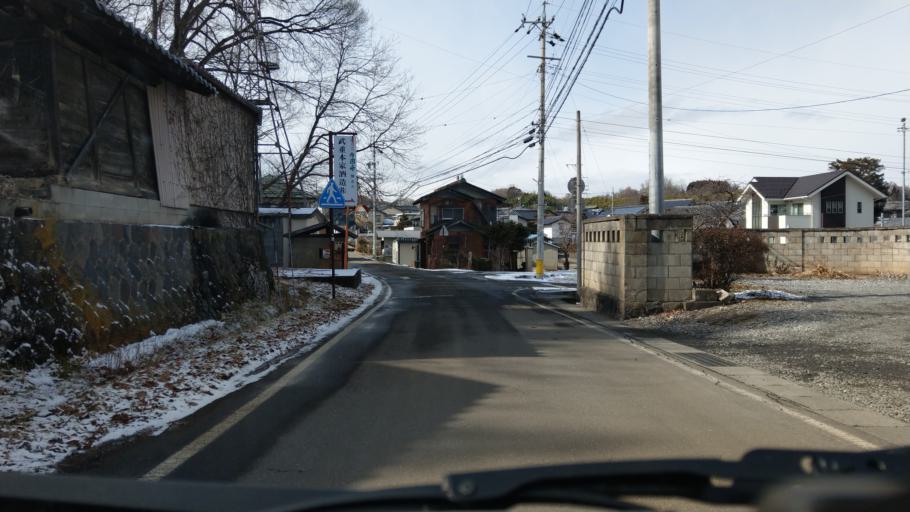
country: JP
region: Nagano
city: Kamimaruko
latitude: 36.2717
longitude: 138.3391
